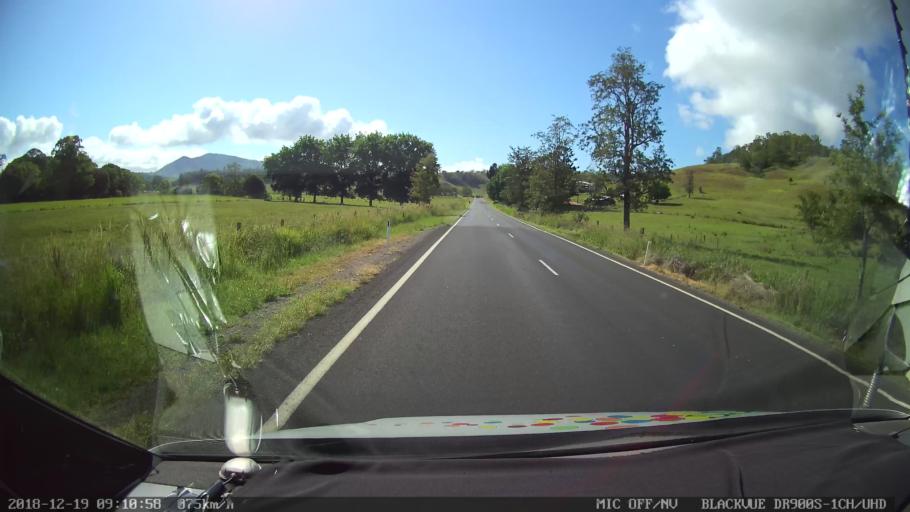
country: AU
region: New South Wales
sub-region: Kyogle
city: Kyogle
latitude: -28.4892
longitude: 152.9339
